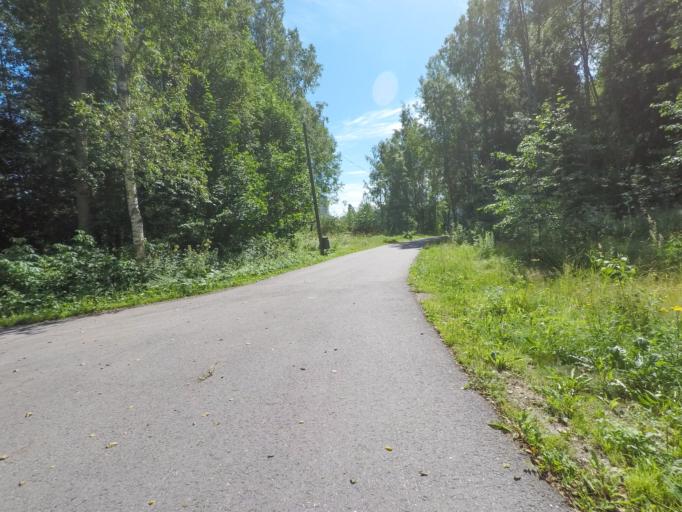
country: FI
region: Uusimaa
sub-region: Helsinki
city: Vantaa
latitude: 60.2149
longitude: 25.0712
